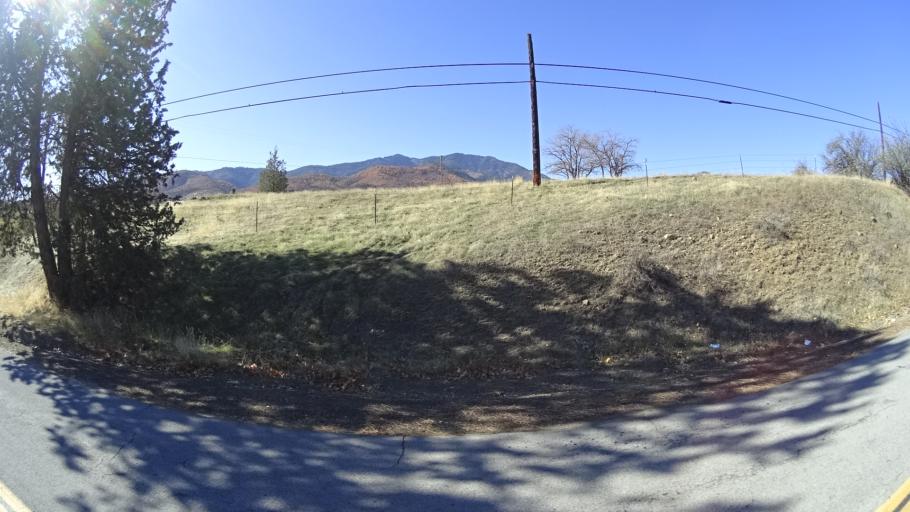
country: US
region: California
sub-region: Siskiyou County
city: Montague
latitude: 41.9198
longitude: -122.5678
